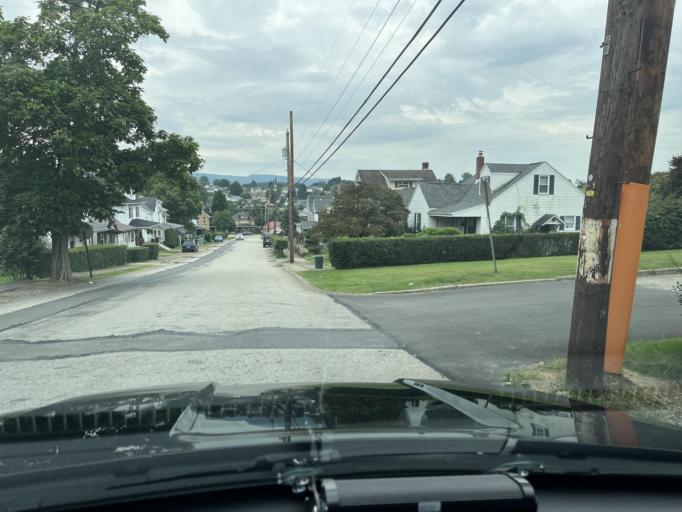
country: US
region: Pennsylvania
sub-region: Fayette County
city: South Uniontown
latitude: 39.8973
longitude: -79.7394
